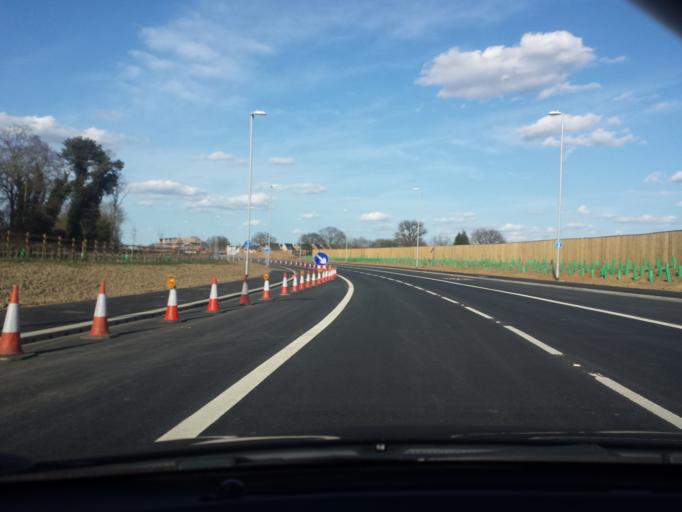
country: GB
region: England
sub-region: Essex
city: Colchester
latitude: 51.9164
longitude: 0.8998
